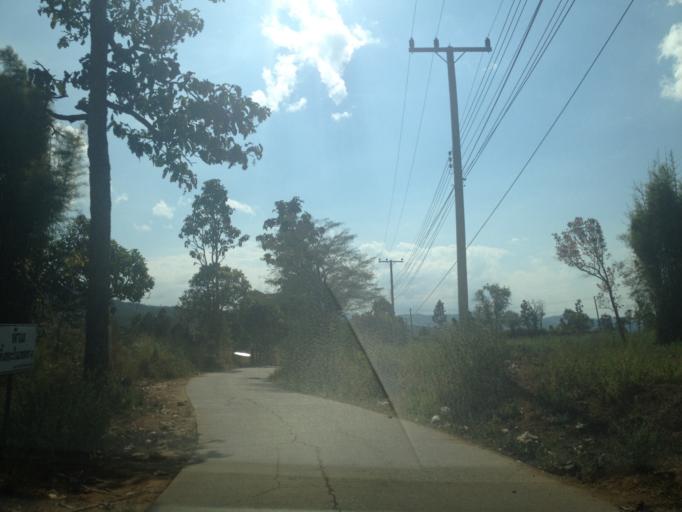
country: TH
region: Mae Hong Son
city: Ban Huai I Huak
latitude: 18.1042
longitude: 98.2177
